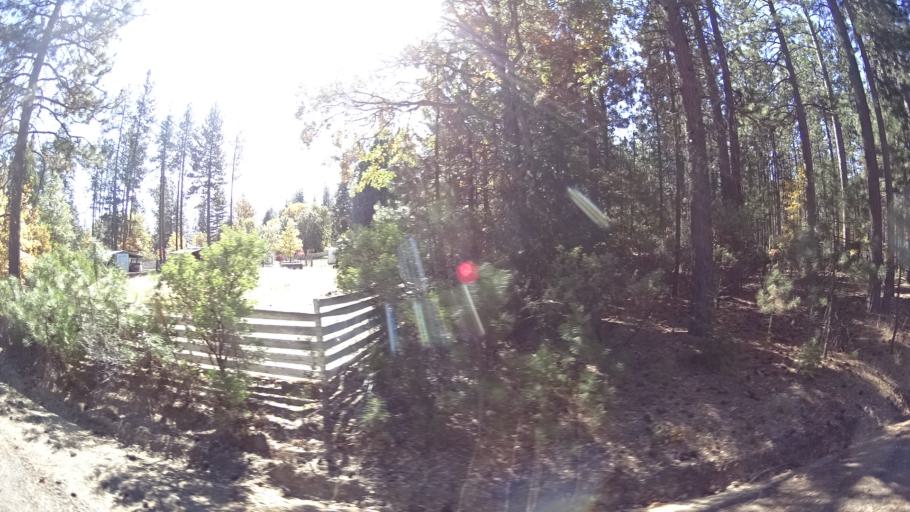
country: US
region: California
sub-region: Siskiyou County
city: Yreka
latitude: 41.5136
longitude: -122.9081
